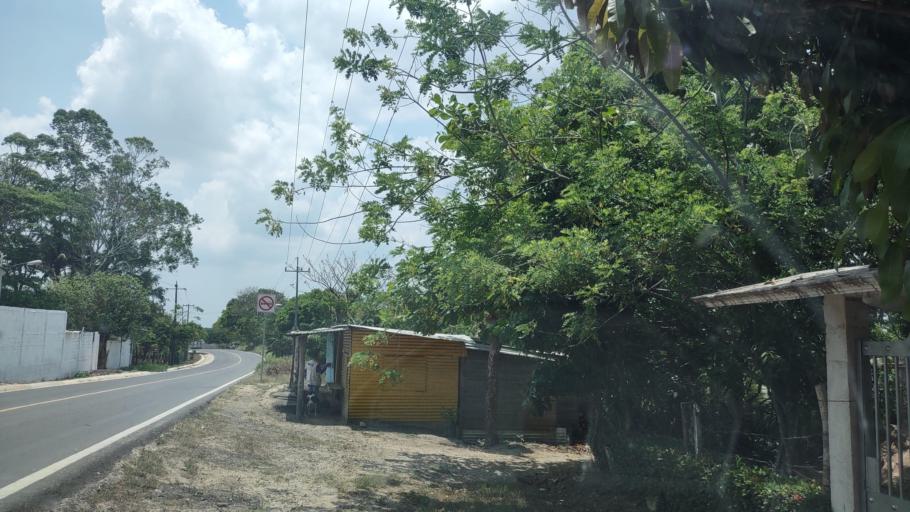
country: MX
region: Veracruz
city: Las Choapas
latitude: 17.9290
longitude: -94.1488
